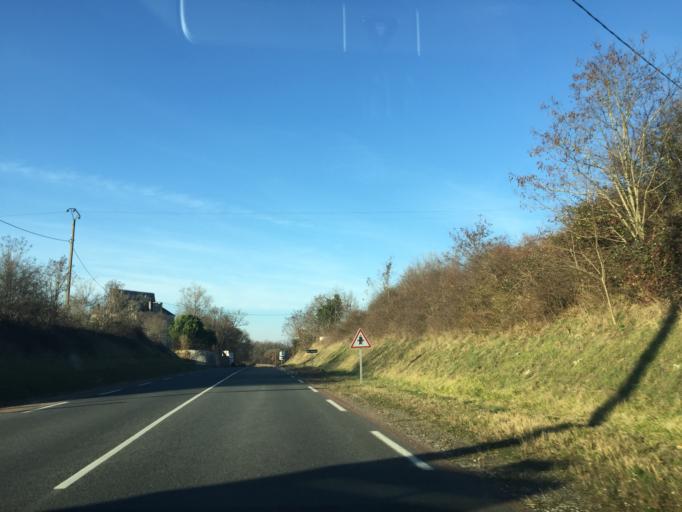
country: FR
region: Aquitaine
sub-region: Departement de la Dordogne
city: Riberac
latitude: 45.1982
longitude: 0.3682
